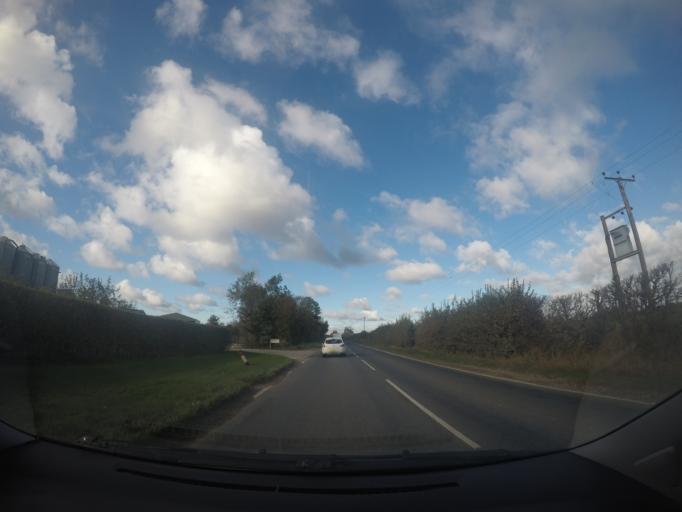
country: GB
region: England
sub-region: City of York
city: Askham Richard
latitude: 53.9920
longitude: -1.2385
